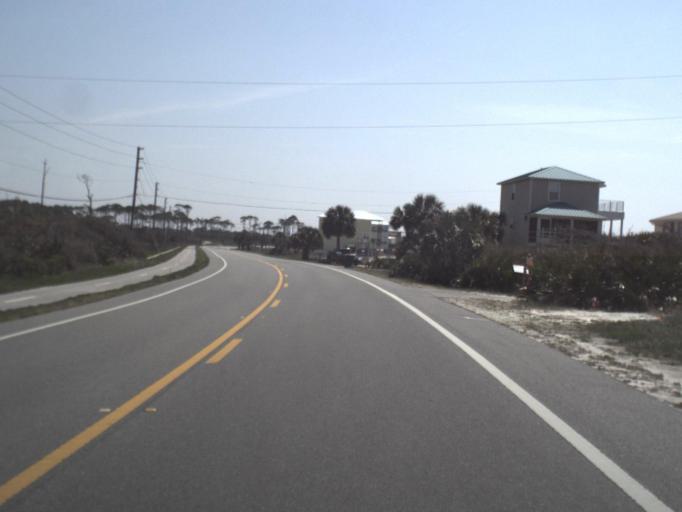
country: US
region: Florida
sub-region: Gulf County
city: Port Saint Joe
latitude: 29.6875
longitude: -85.3710
